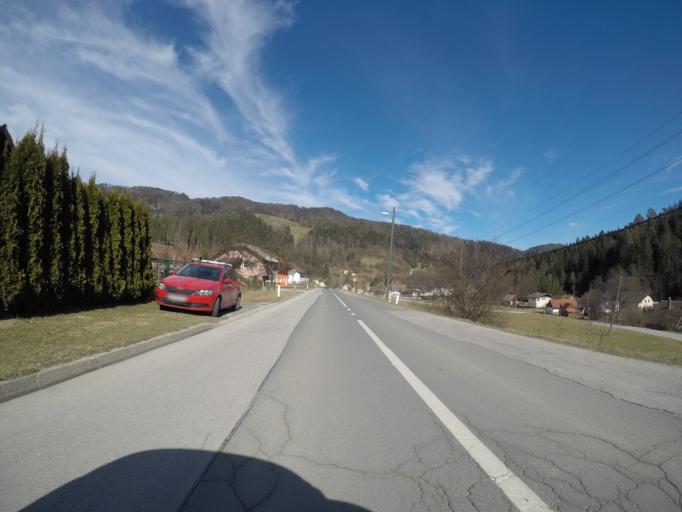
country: SI
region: Lovrenc na Pohorju
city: Lovrenc na Pohorju
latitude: 46.5481
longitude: 15.4038
